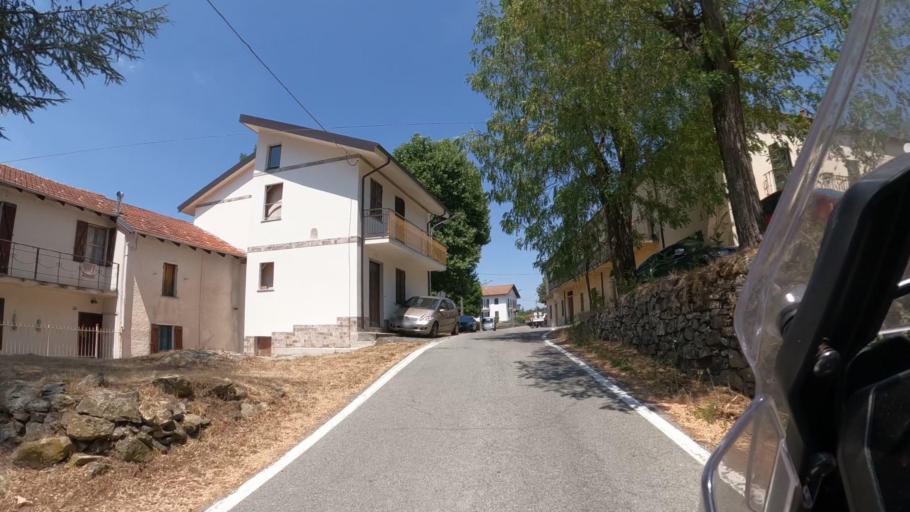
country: IT
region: Piedmont
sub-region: Provincia di Alessandria
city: Ponzone
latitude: 44.5515
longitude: 8.4825
